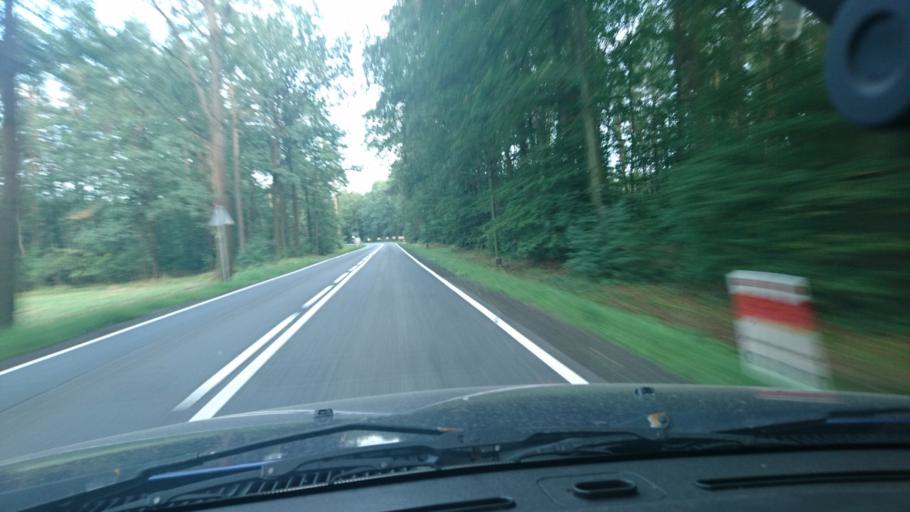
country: PL
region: Opole Voivodeship
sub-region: Powiat oleski
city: Olesno
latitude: 50.8514
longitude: 18.4680
